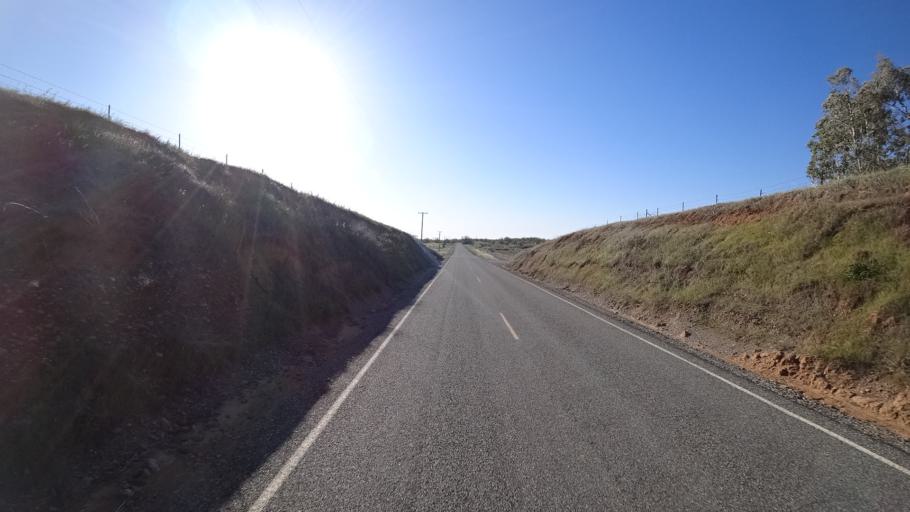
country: US
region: California
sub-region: Glenn County
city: Orland
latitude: 39.8242
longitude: -122.3327
